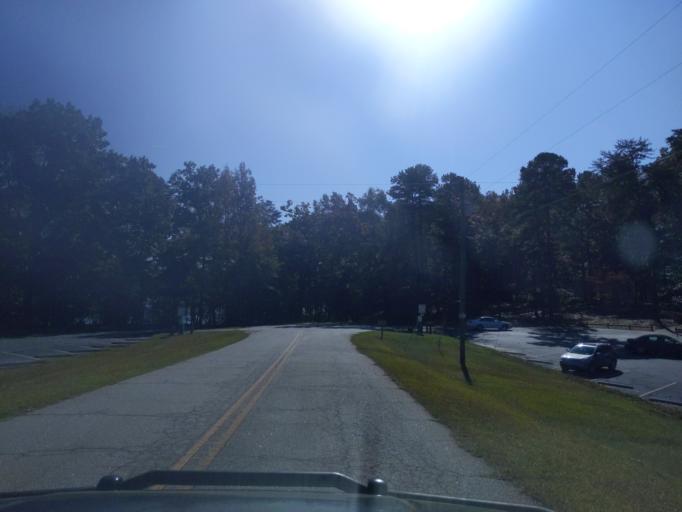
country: US
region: Georgia
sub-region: Franklin County
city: Gumlog
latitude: 34.4929
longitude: -83.0630
